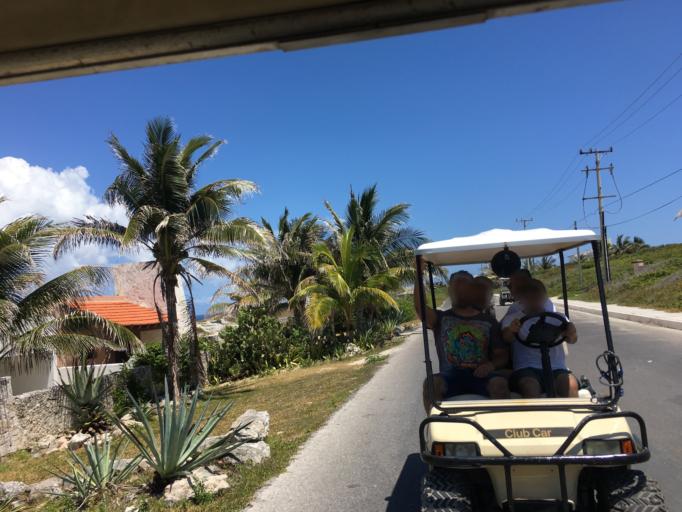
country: MX
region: Quintana Roo
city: Isla Mujeres
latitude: 21.2067
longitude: -86.7158
